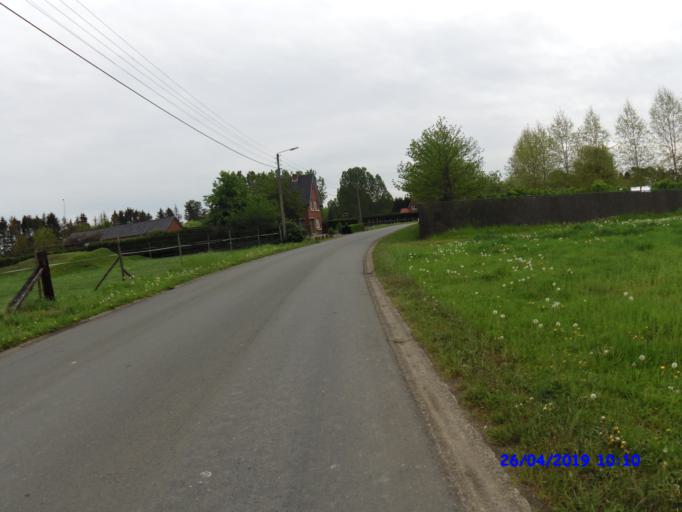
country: BE
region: Flanders
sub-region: Provincie Limburg
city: Lummen
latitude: 50.9611
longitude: 5.2297
